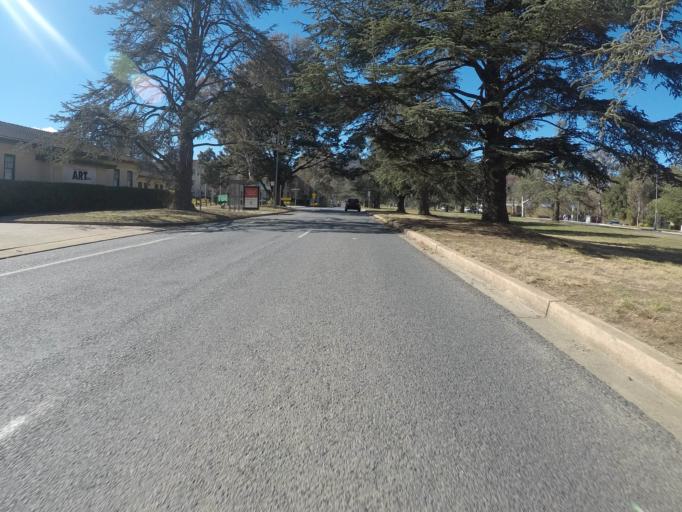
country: AU
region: Australian Capital Territory
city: Canberra
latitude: -35.2783
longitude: 149.1378
